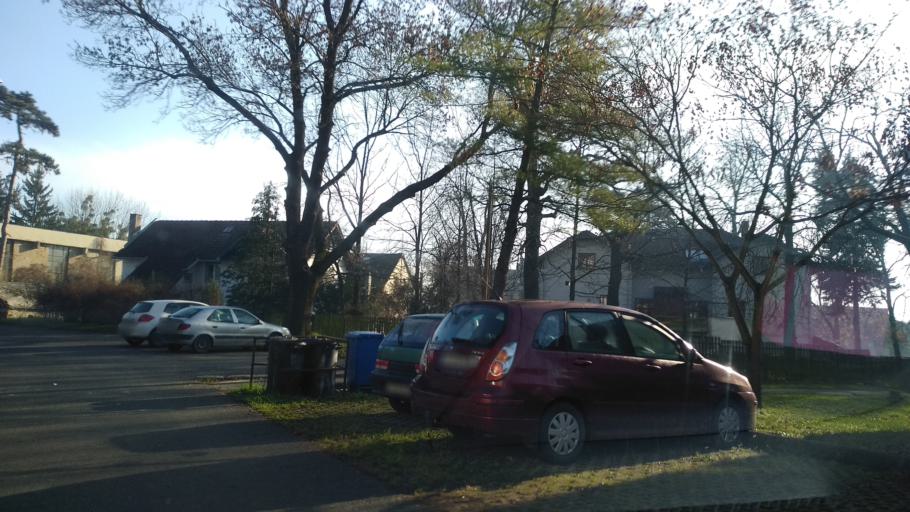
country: HU
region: Somogy
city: Barcs
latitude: 45.9583
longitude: 17.4510
